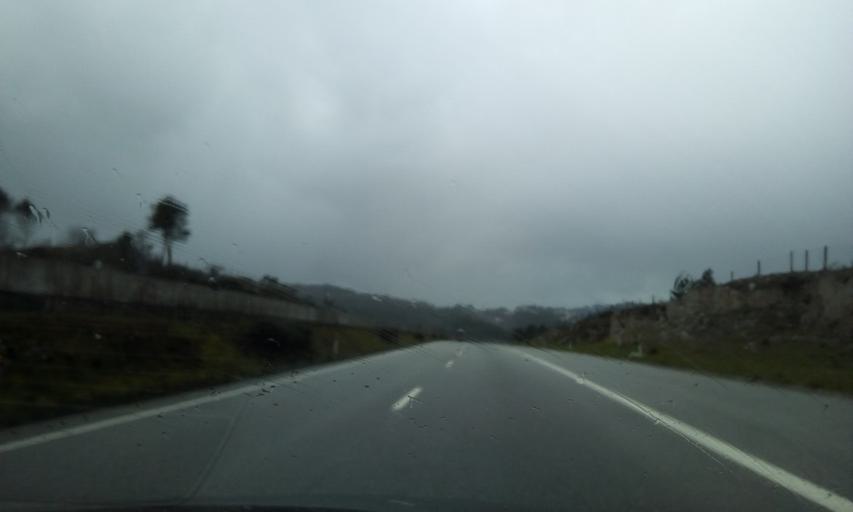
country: PT
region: Viseu
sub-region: Mangualde
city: Mangualde
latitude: 40.6139
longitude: -7.7029
